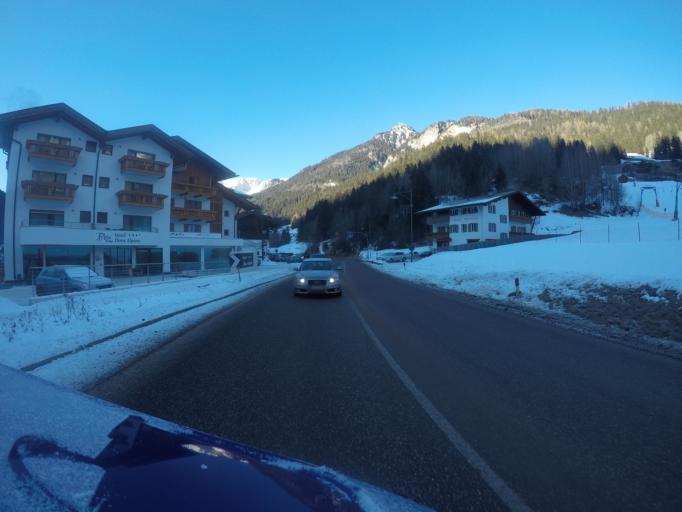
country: IT
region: Trentino-Alto Adige
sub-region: Provincia di Trento
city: Campitello di Fassa
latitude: 46.4734
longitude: 11.7363
